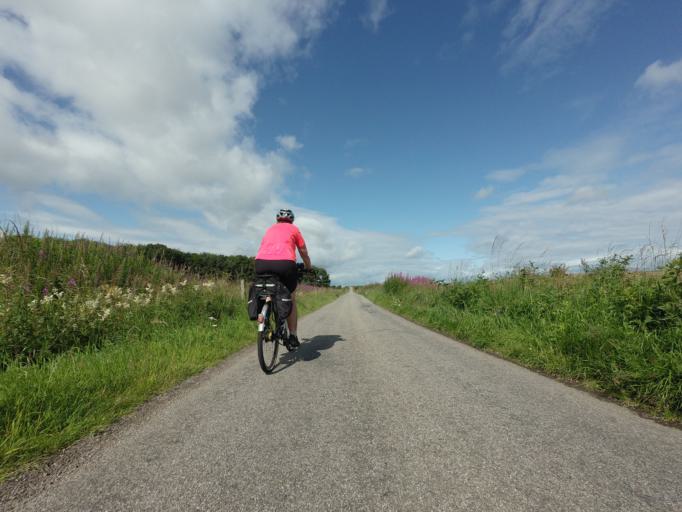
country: GB
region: Scotland
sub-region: Moray
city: Burghead
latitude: 57.6532
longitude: -3.4673
